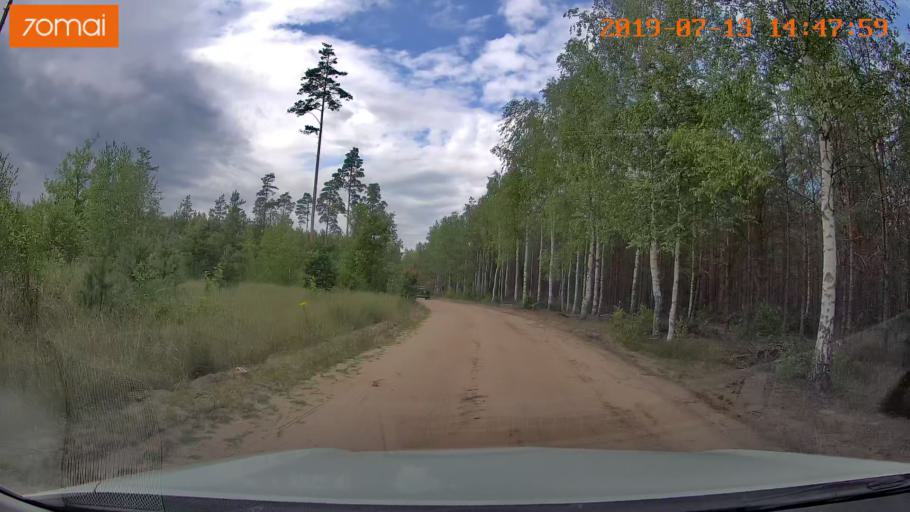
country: BY
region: Mogilev
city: Asipovichy
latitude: 53.2039
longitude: 28.7520
